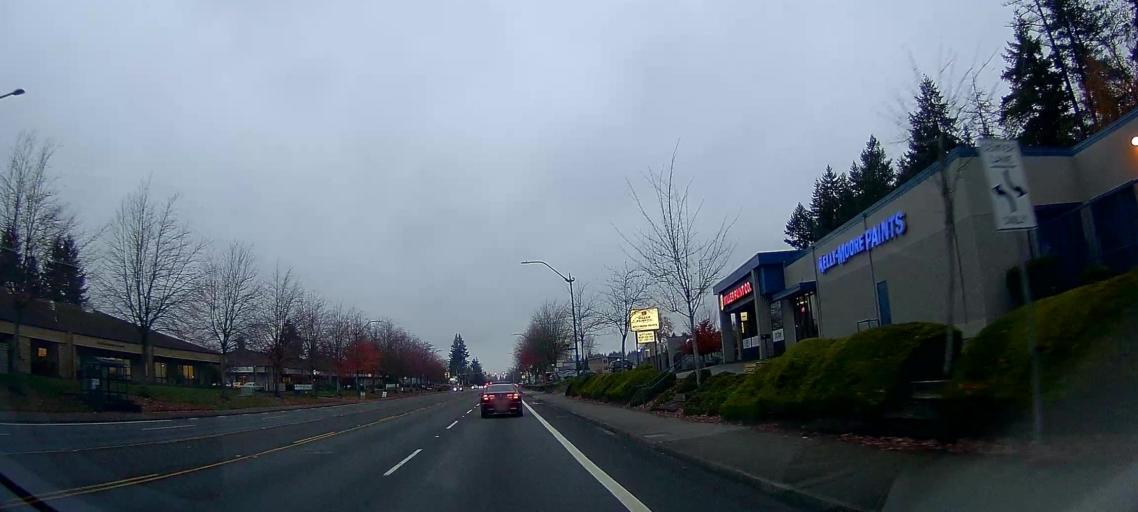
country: US
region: Washington
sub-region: Thurston County
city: Lacey
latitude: 47.0476
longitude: -122.8402
